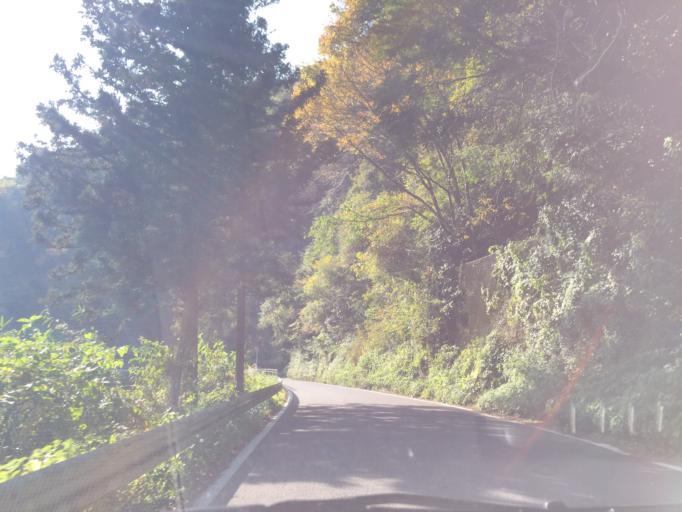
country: JP
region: Gifu
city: Minokamo
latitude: 35.5463
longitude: 137.1187
